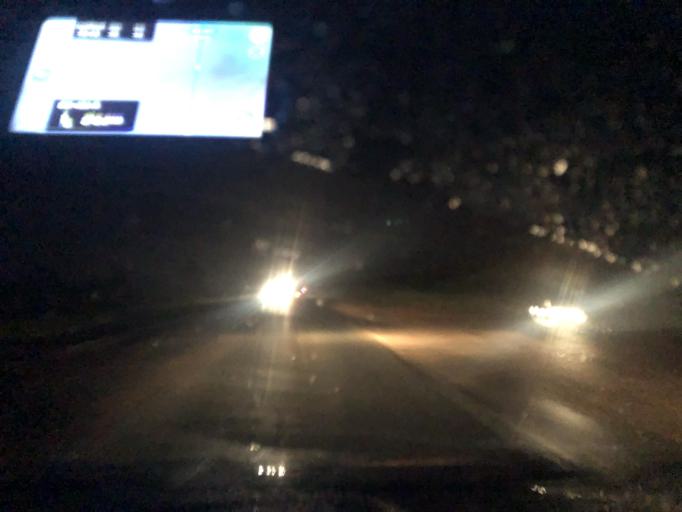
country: BR
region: Santa Catarina
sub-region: Guaramirim
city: Guaramirim
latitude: -26.4523
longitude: -48.8962
